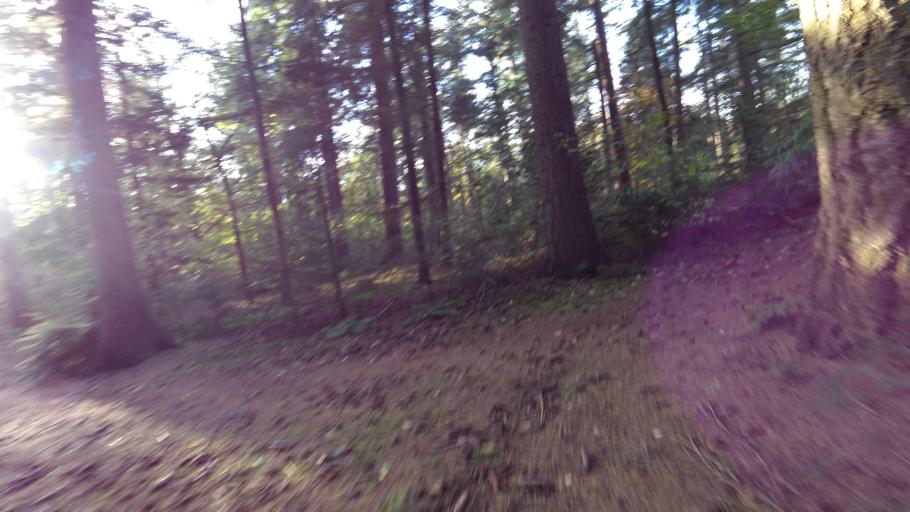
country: NL
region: Gelderland
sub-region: Gemeente Ede
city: Lunteren
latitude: 52.0845
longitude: 5.6425
